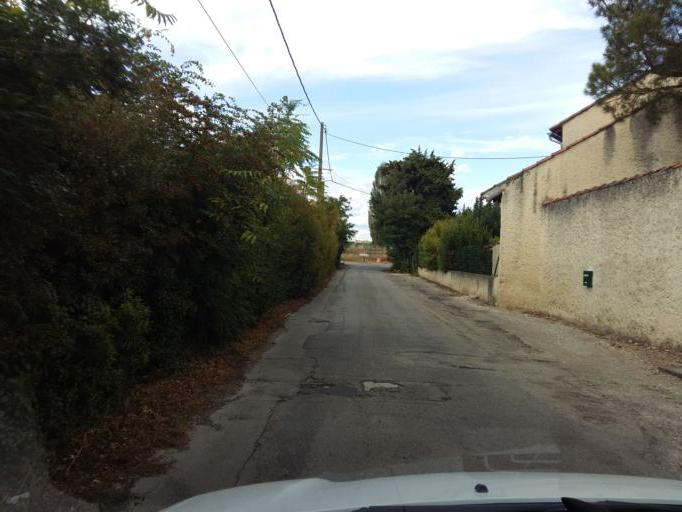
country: FR
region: Provence-Alpes-Cote d'Azur
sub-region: Departement du Vaucluse
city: Carpentras
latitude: 44.0387
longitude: 5.0350
